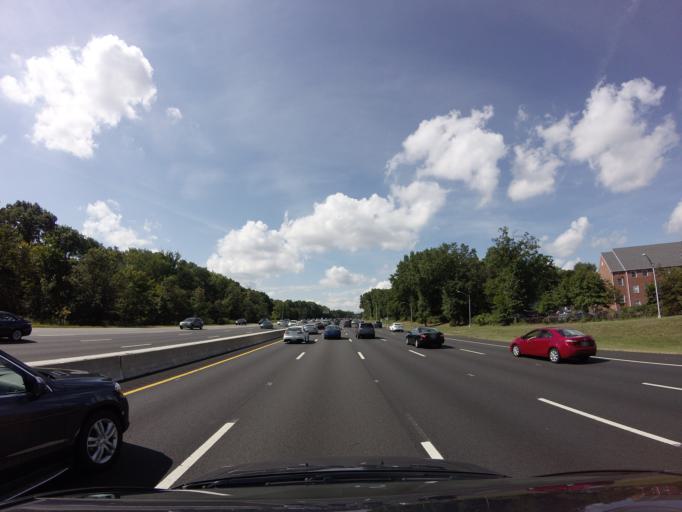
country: US
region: New Jersey
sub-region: Union County
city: Winfield
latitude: 40.6390
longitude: -74.2910
